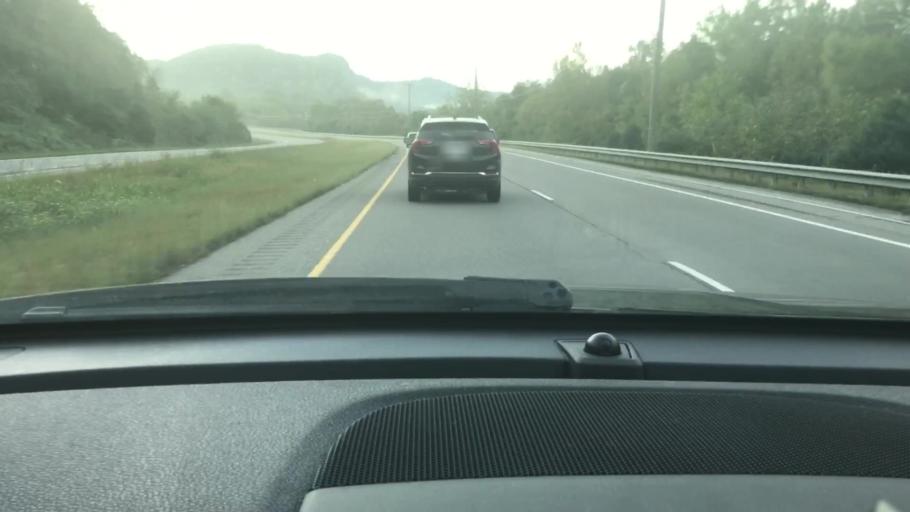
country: US
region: Tennessee
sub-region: Cheatham County
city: Ashland City
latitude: 36.2078
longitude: -86.9527
